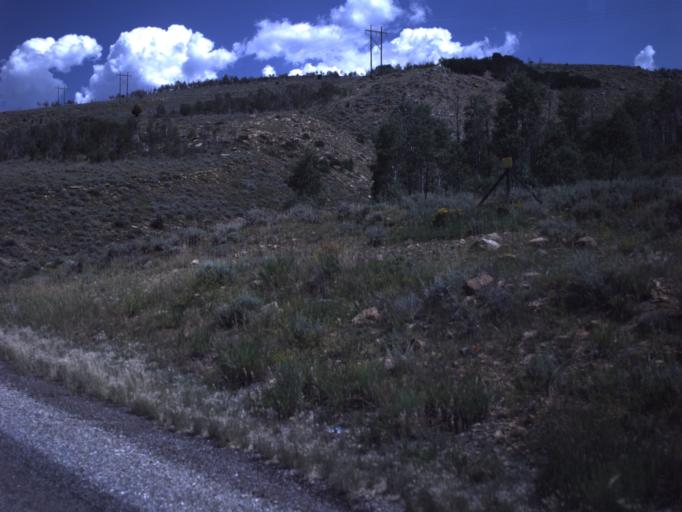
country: US
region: Utah
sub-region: Carbon County
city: Helper
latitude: 39.8194
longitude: -111.1353
